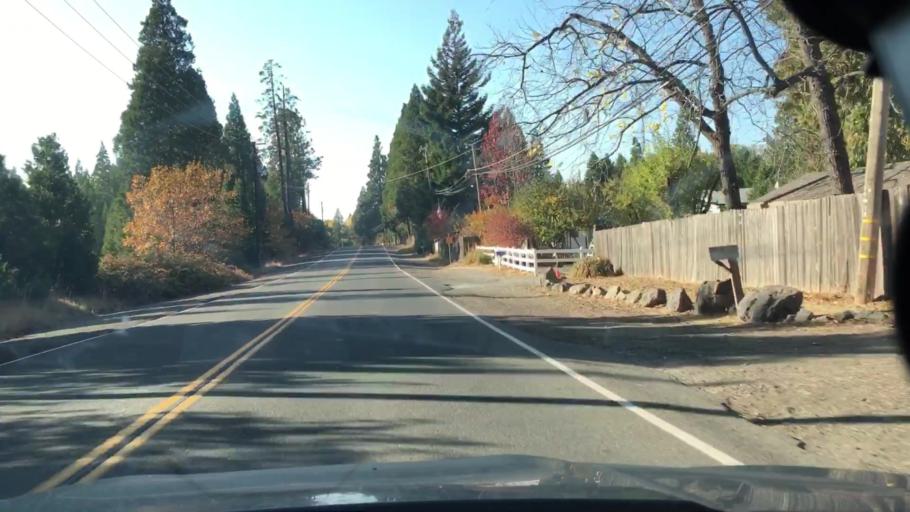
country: US
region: California
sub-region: El Dorado County
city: Camino
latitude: 38.7405
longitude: -120.6907
